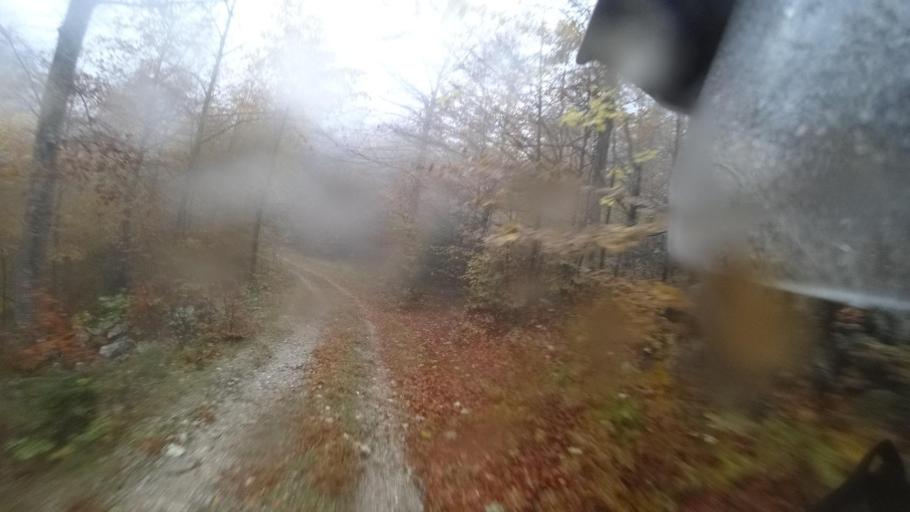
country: HR
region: Primorsko-Goranska
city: Vrbovsko
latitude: 45.2817
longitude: 14.9689
